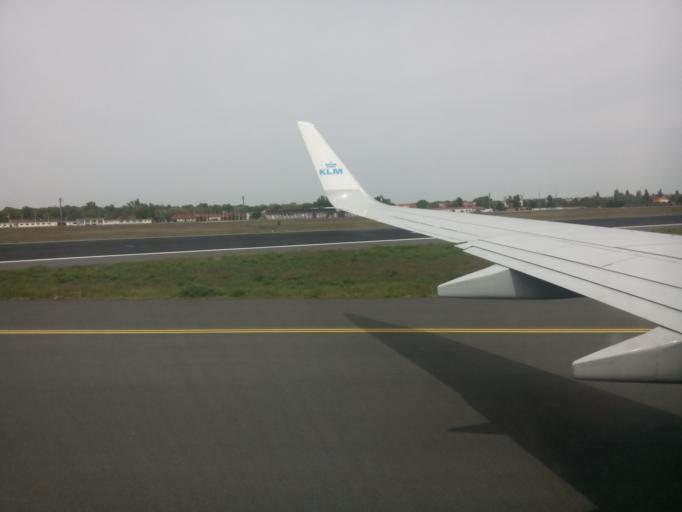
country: DE
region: Berlin
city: Tegel
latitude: 52.5601
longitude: 13.2981
